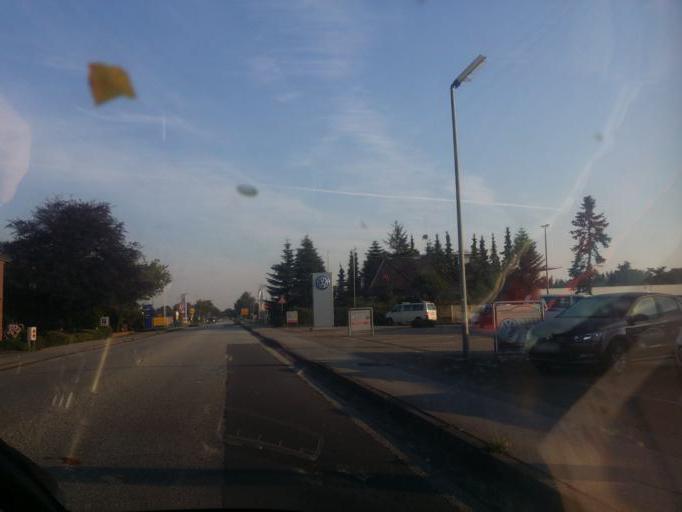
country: DE
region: Schleswig-Holstein
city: Breklum
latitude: 54.6076
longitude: 8.9801
